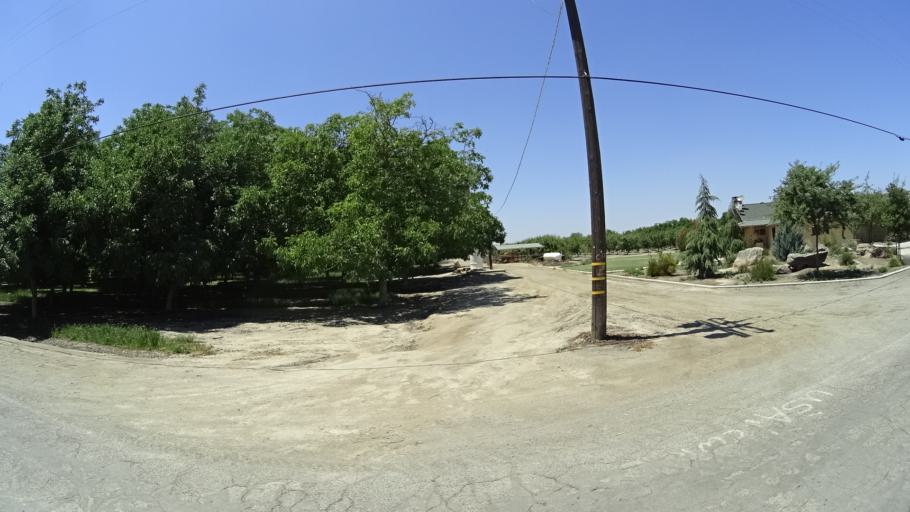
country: US
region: California
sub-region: Kings County
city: Lucerne
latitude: 36.4083
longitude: -119.6189
